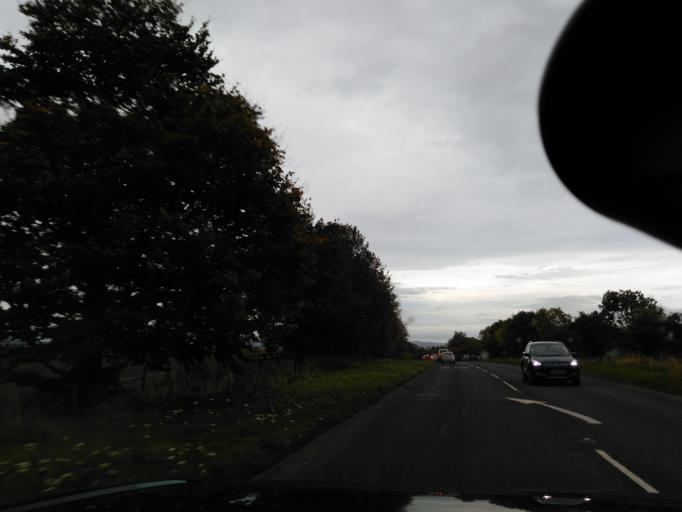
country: GB
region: England
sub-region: North Yorkshire
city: Northallerton
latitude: 54.3238
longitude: -1.4684
